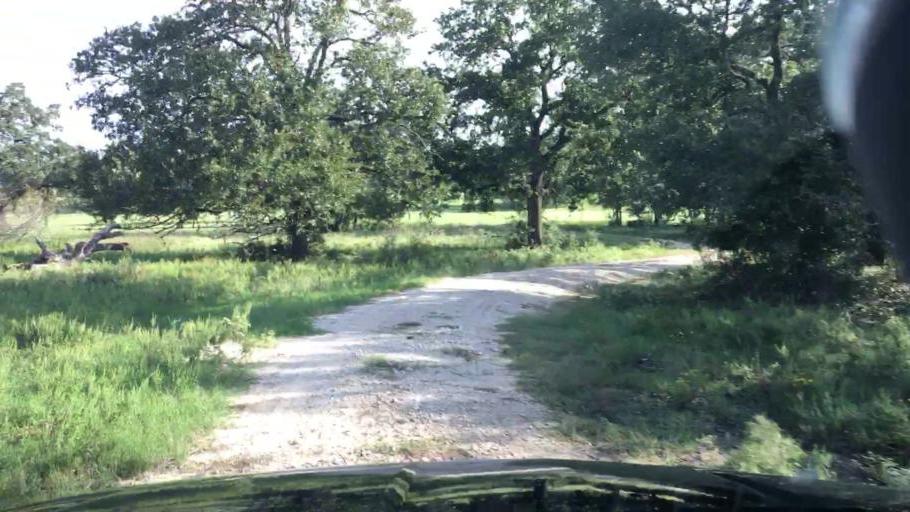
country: US
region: Texas
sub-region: Burleson County
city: Somerville
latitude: 30.3050
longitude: -96.7304
